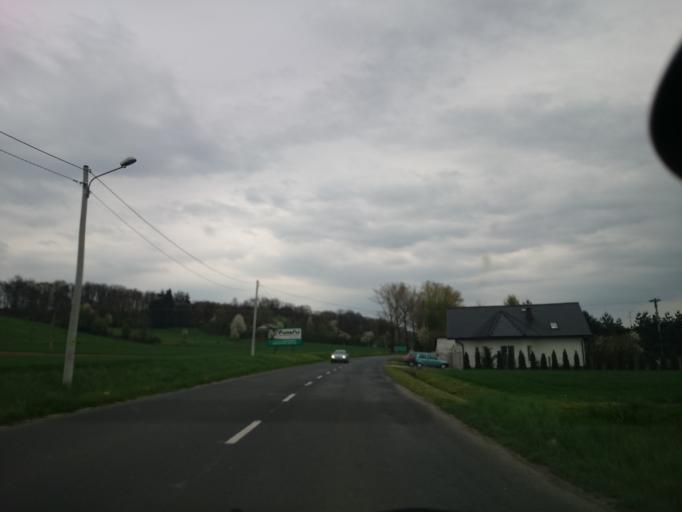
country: PL
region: Opole Voivodeship
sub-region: Powiat nyski
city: Nysa
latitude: 50.4095
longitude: 17.3395
